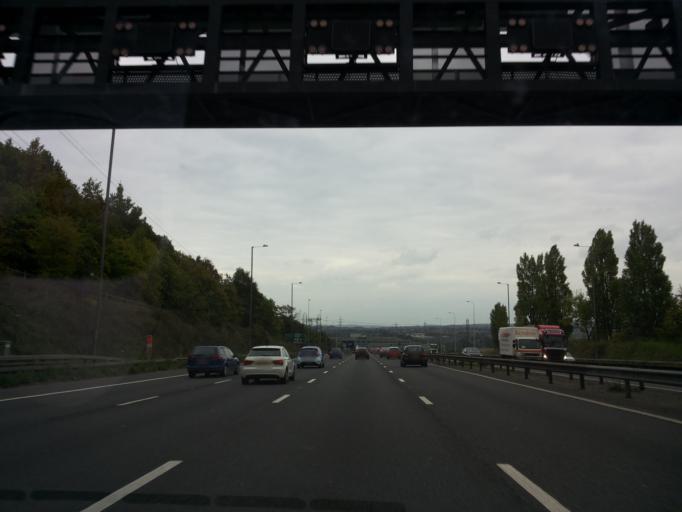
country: GB
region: England
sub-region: Kent
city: Swanscombe
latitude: 51.4305
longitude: 0.3026
